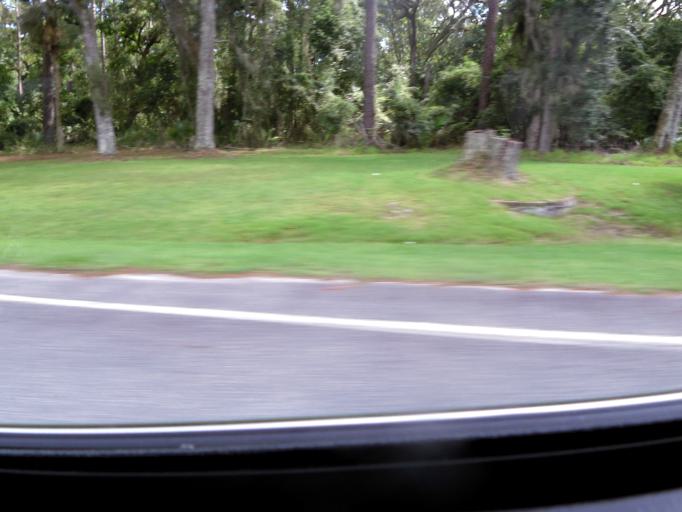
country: US
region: Georgia
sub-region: Glynn County
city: Dock Junction
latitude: 31.1672
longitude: -81.5505
